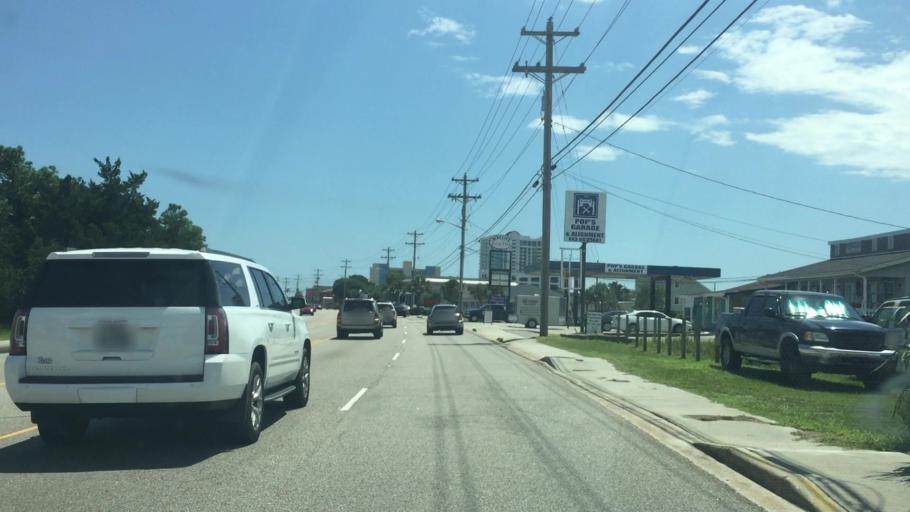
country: US
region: South Carolina
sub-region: Horry County
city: North Myrtle Beach
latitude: 33.8336
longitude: -78.6448
